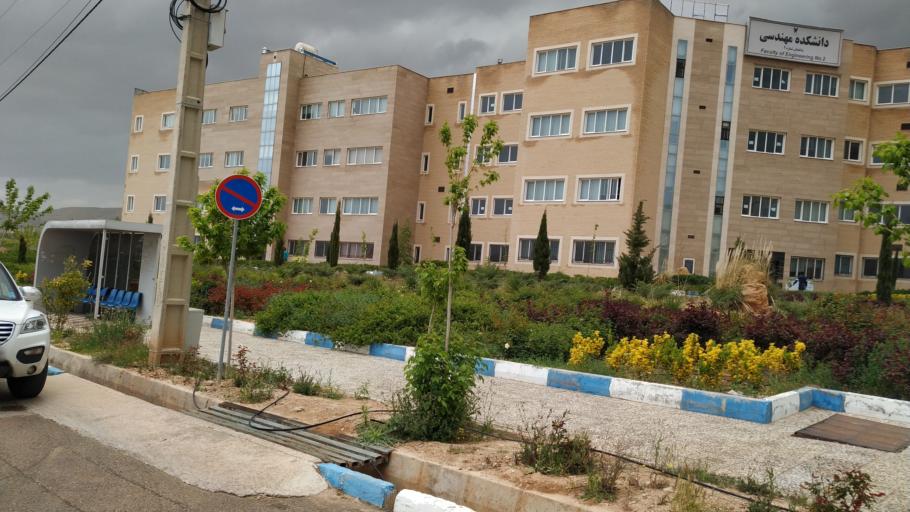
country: IR
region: Fars
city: Shiraz
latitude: 29.7623
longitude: 52.4849
